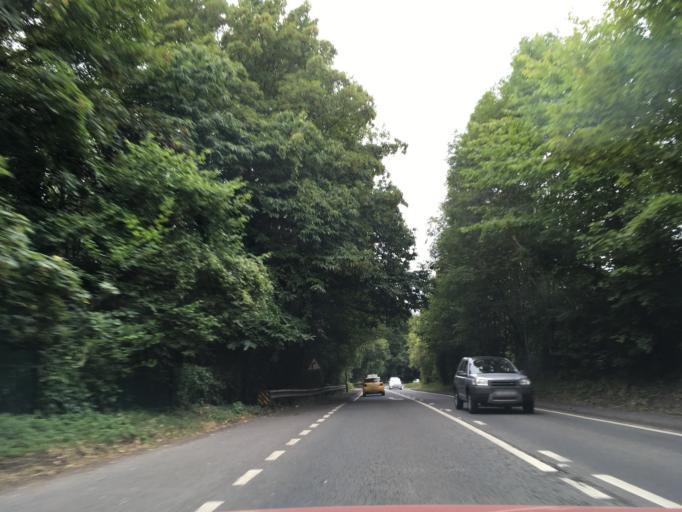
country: GB
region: Wales
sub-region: Monmouthshire
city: Gilwern
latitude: 51.8402
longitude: -3.0923
